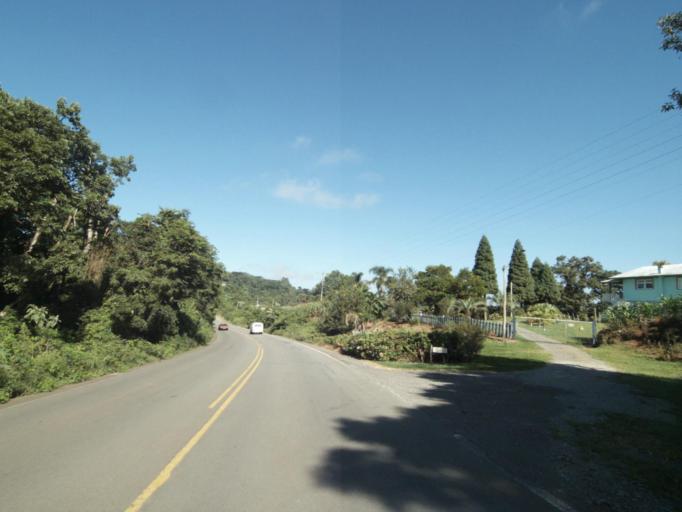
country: BR
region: Rio Grande do Sul
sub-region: Bento Goncalves
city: Bento Goncalves
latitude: -29.1204
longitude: -51.5520
